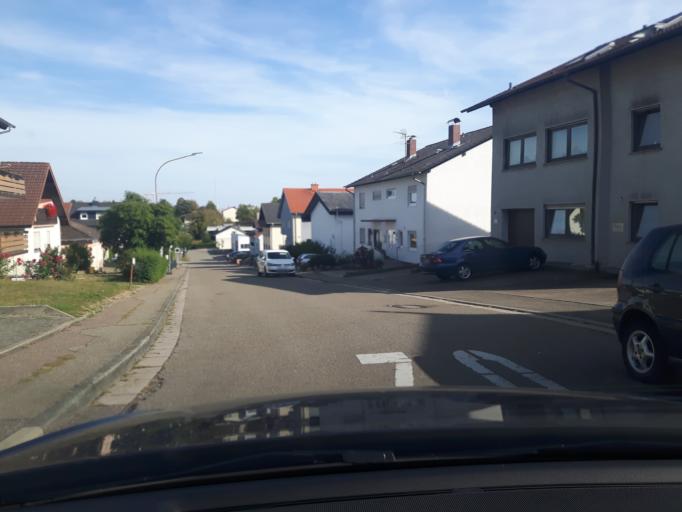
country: DE
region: Baden-Wuerttemberg
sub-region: Karlsruhe Region
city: Sinsheim
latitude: 49.2454
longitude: 8.8717
